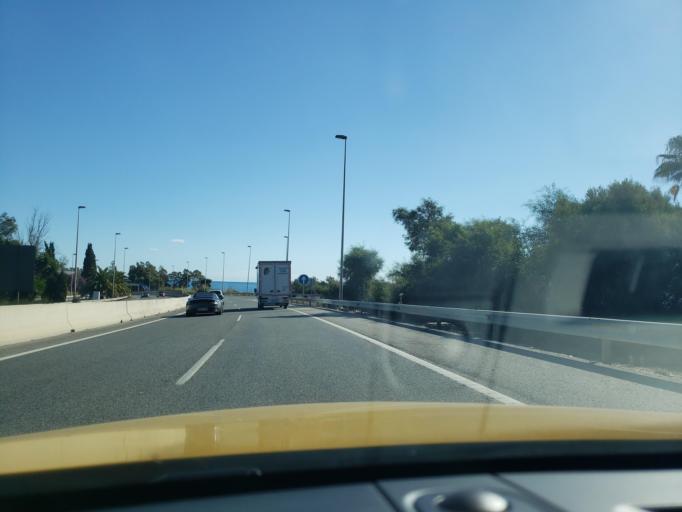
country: ES
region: Andalusia
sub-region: Provincia de Malaga
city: Marbella
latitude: 36.5094
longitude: -4.8613
